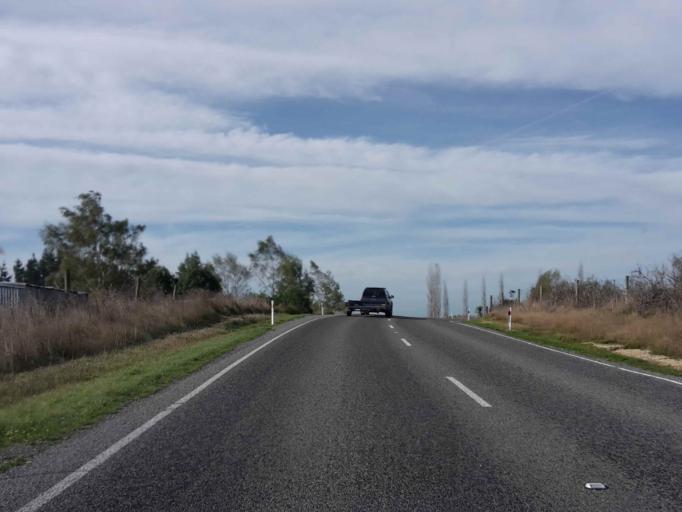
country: NZ
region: Canterbury
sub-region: Timaru District
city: Pleasant Point
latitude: -44.1237
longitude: 171.1043
